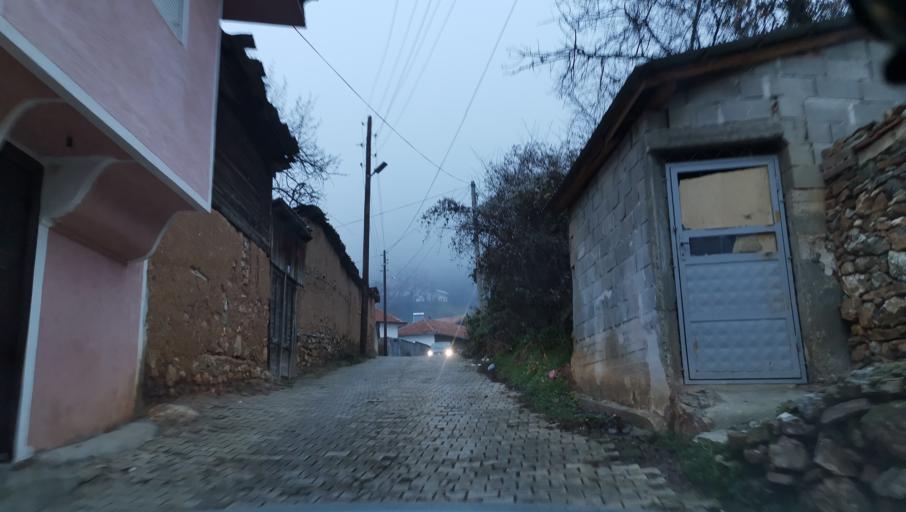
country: MK
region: Debar
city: Debar
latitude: 41.5271
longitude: 20.5283
